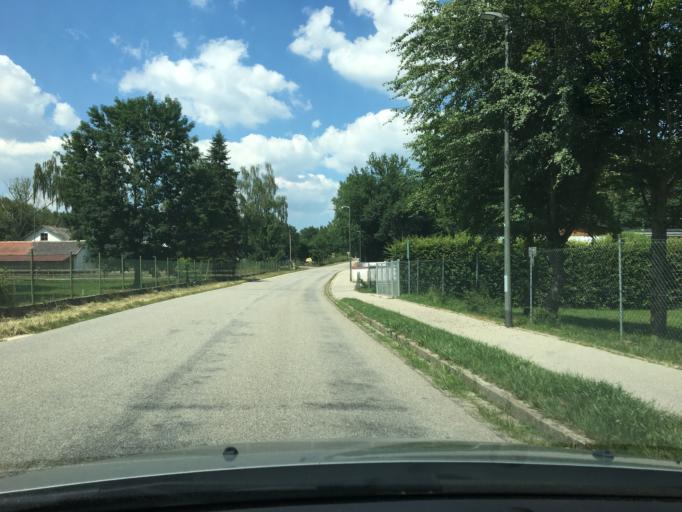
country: DE
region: Bavaria
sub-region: Upper Bavaria
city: Neumarkt-Sankt Veit
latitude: 48.3703
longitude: 12.5063
